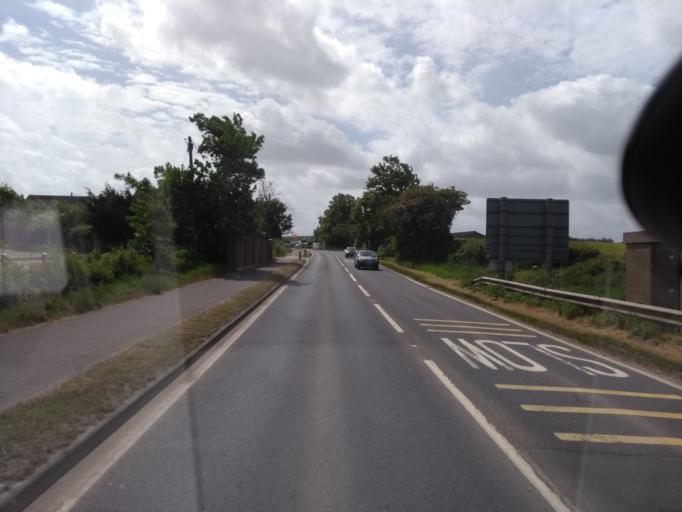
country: GB
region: England
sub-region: Somerset
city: Bridgwater
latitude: 51.1441
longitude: -3.0580
